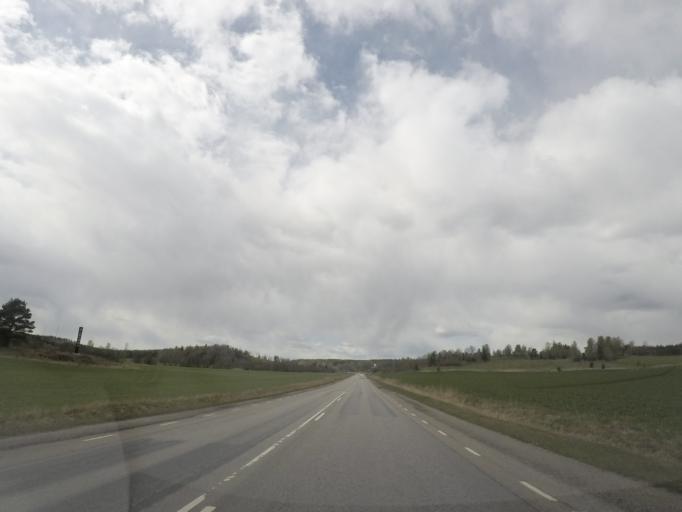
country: SE
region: Soedermanland
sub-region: Nykopings Kommun
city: Olstorp
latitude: 58.7436
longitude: 16.5712
